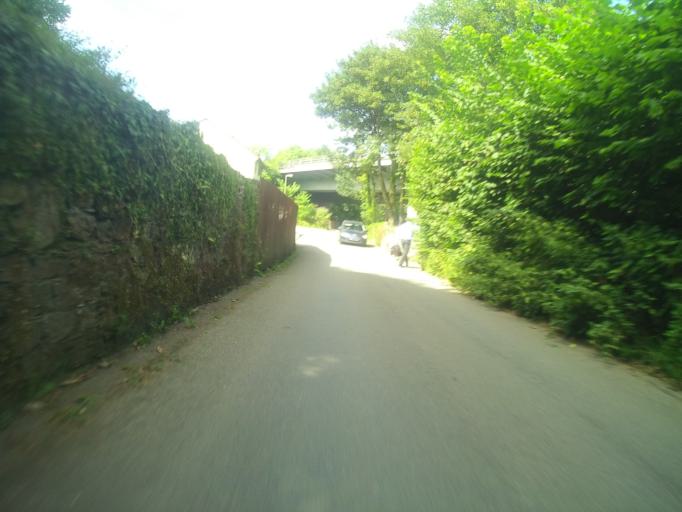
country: GB
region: England
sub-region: Devon
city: Buckfastleigh
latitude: 50.4808
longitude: -3.7710
